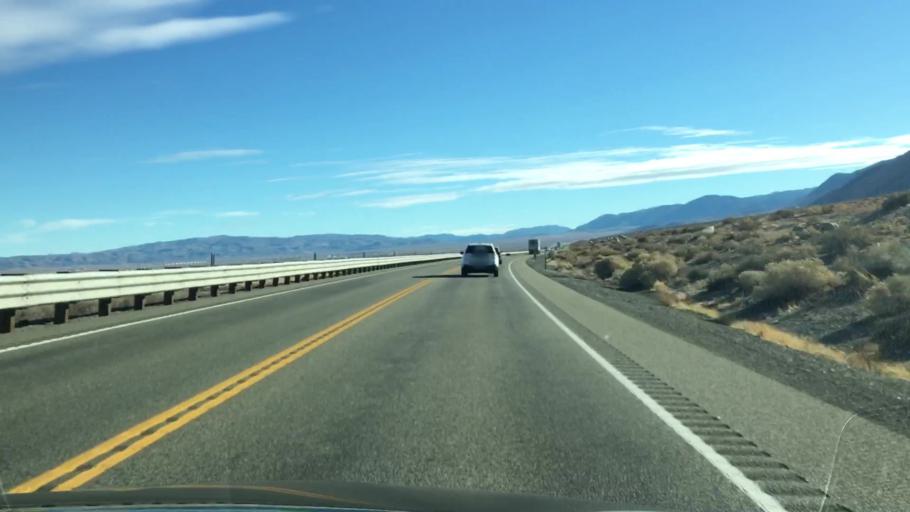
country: US
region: Nevada
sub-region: Mineral County
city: Hawthorne
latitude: 38.6065
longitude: -118.7128
